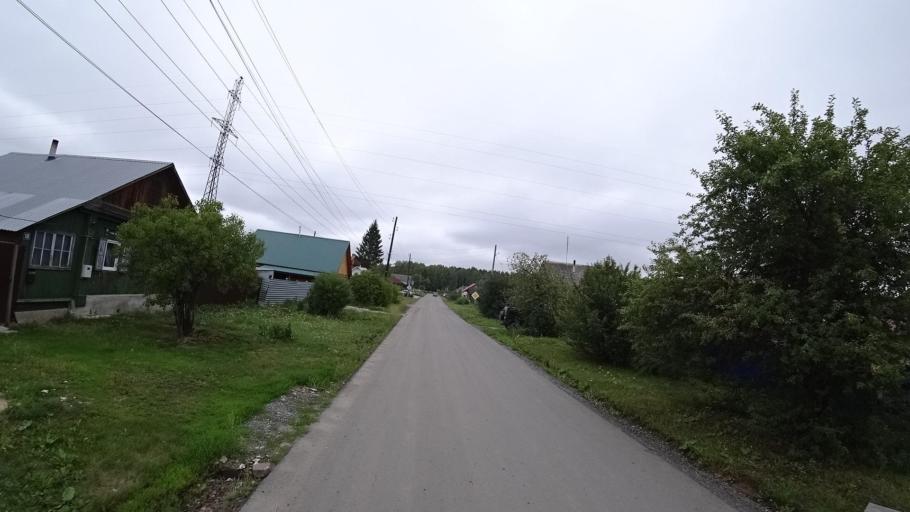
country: RU
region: Sverdlovsk
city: Kamyshlov
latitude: 56.8445
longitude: 62.7512
